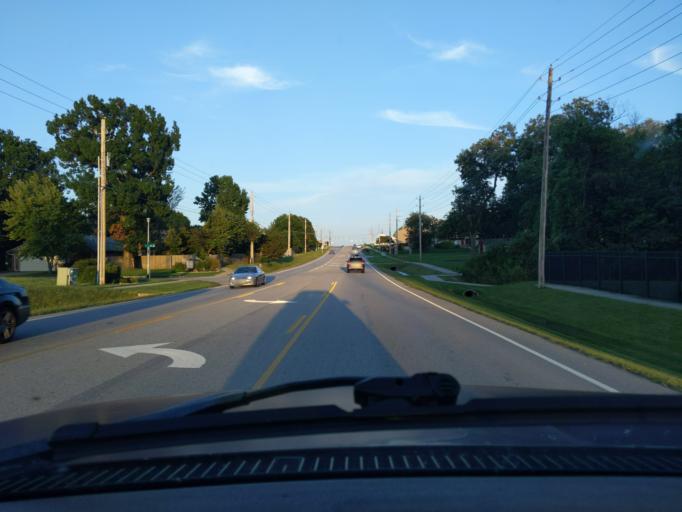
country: US
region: Oklahoma
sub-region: Tulsa County
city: Jenks
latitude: 36.0464
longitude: -95.9092
